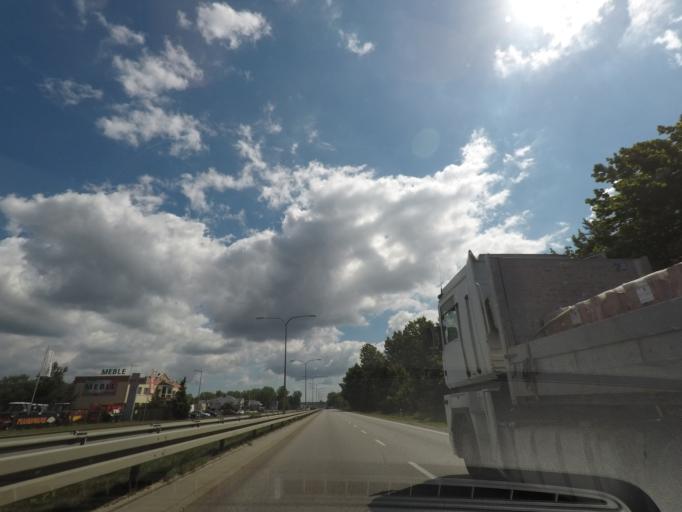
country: PL
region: Pomeranian Voivodeship
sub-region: Powiat wejherowski
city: Bolszewo
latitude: 54.6089
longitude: 18.2044
